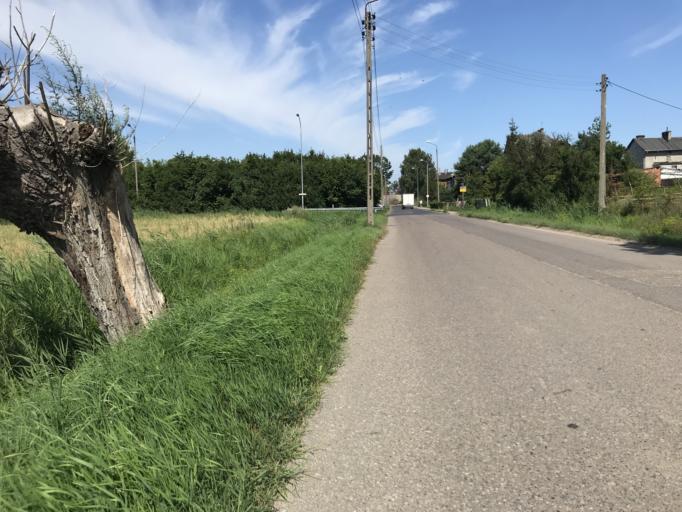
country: PL
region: Pomeranian Voivodeship
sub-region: Gdansk
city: Gdansk
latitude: 54.3341
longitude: 18.6785
